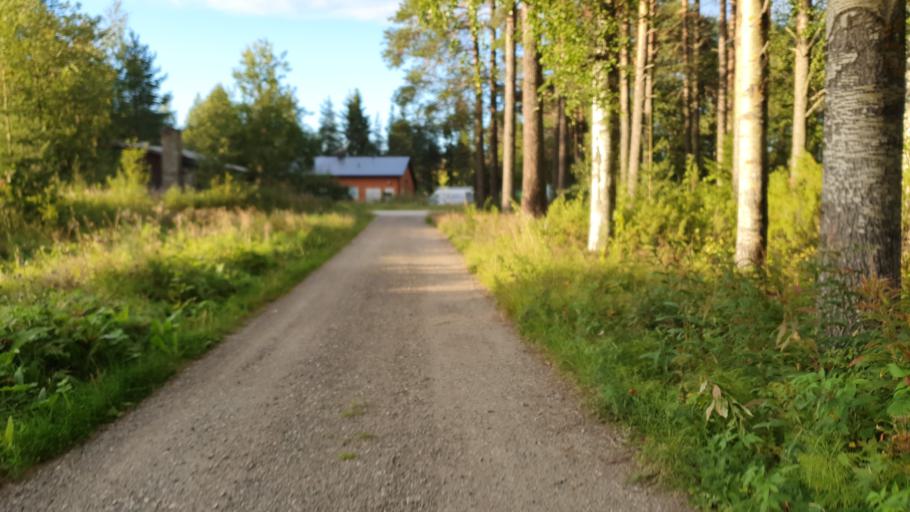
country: FI
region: Kainuu
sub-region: Kehys-Kainuu
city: Kuhmo
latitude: 64.1294
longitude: 29.4931
